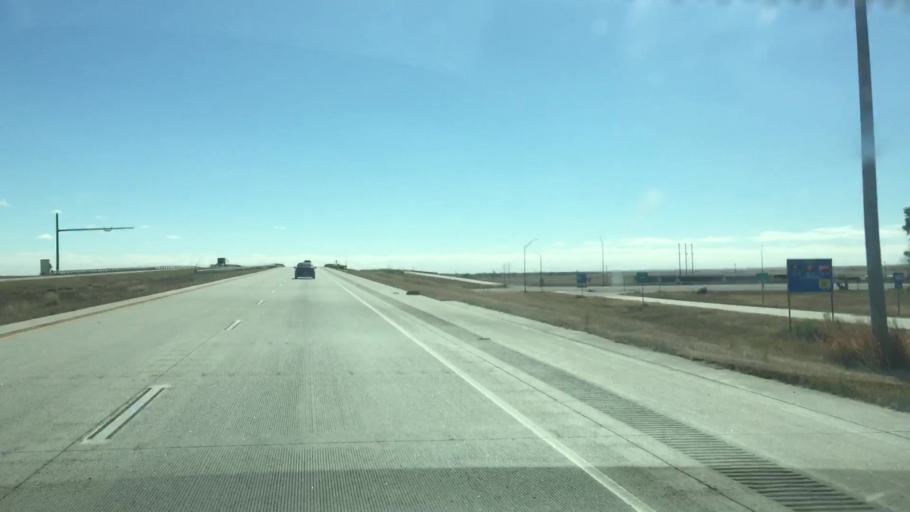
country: US
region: Colorado
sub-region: Lincoln County
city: Limon
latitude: 39.2661
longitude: -103.6707
